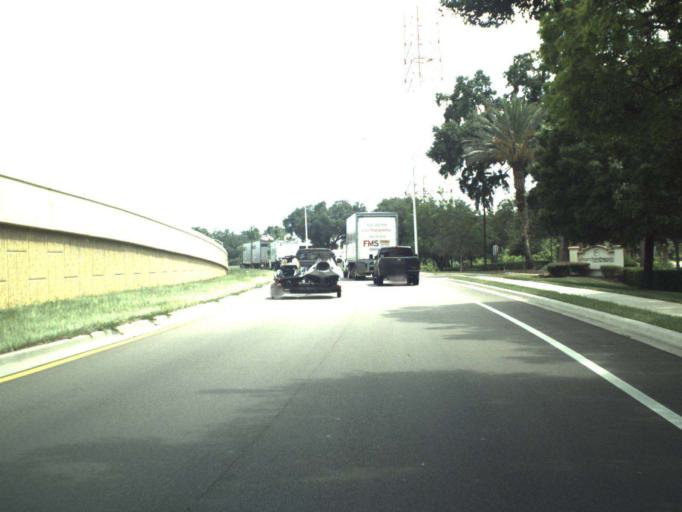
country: US
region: Florida
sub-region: Orange County
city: Fairview Shores
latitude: 28.5960
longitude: -81.4191
